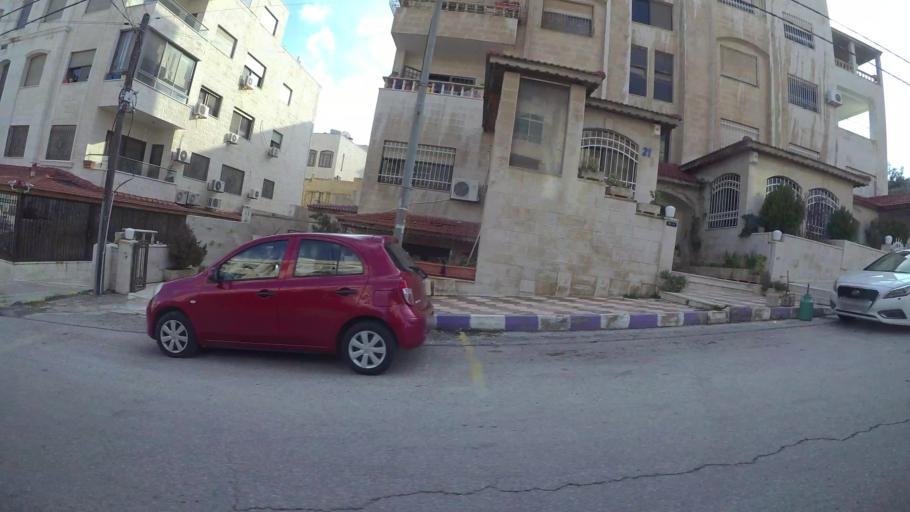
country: JO
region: Amman
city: Al Jubayhah
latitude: 31.9832
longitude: 35.8556
